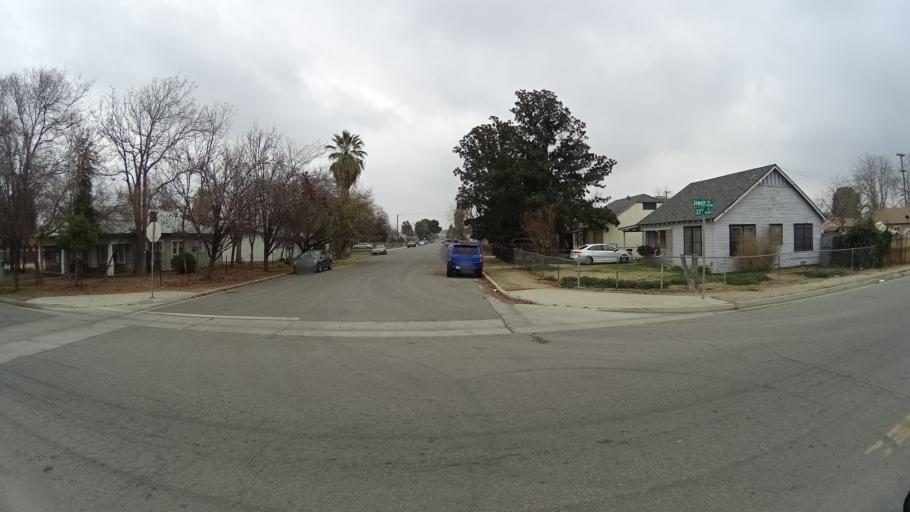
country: US
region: California
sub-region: Kern County
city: Bakersfield
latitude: 35.3892
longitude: -119.0143
